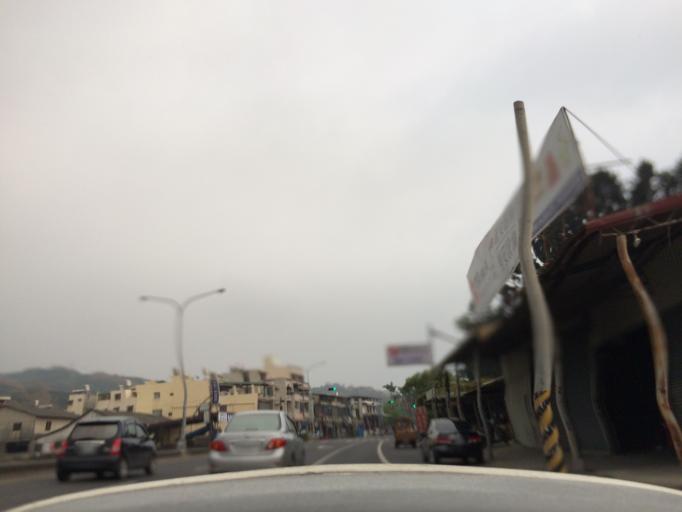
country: TW
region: Taiwan
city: Zhongxing New Village
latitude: 24.0308
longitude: 120.6965
